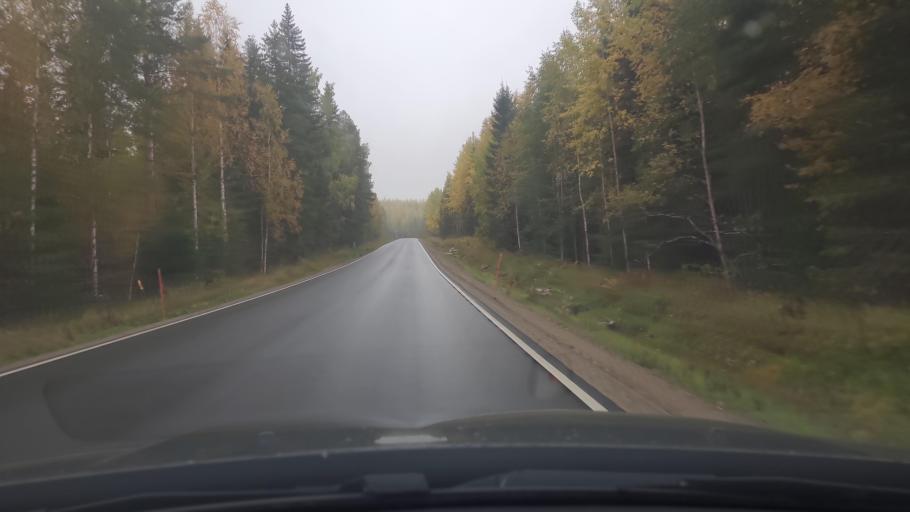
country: FI
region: Northern Savo
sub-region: Varkaus
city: Kangaslampi
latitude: 62.4574
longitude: 28.2687
